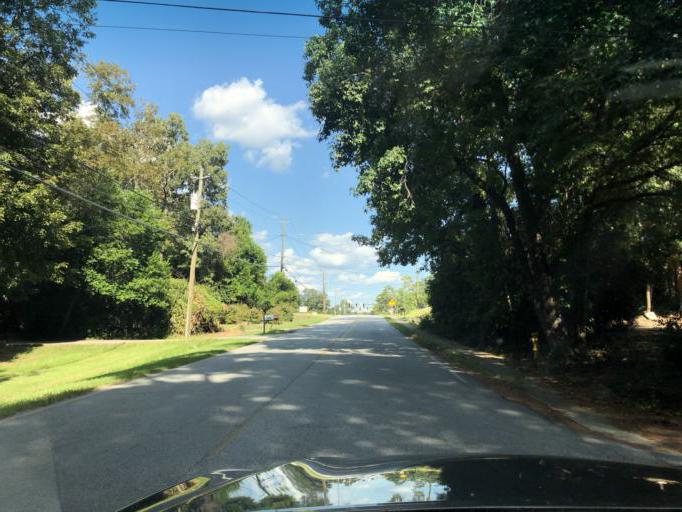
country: US
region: Georgia
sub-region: Muscogee County
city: Columbus
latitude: 32.5396
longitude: -84.9265
